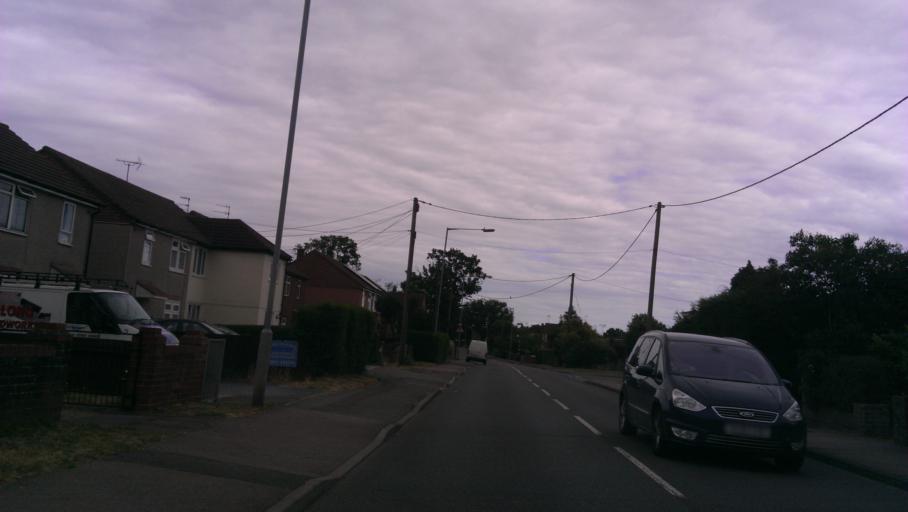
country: GB
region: England
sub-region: Essex
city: Eight Ash Green
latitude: 51.8792
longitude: 0.8367
